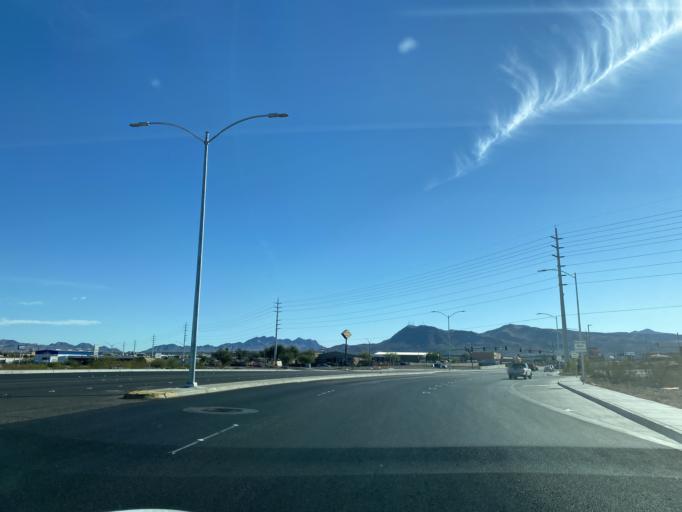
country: US
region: Nevada
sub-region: Clark County
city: Henderson
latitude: 36.0655
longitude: -115.0274
